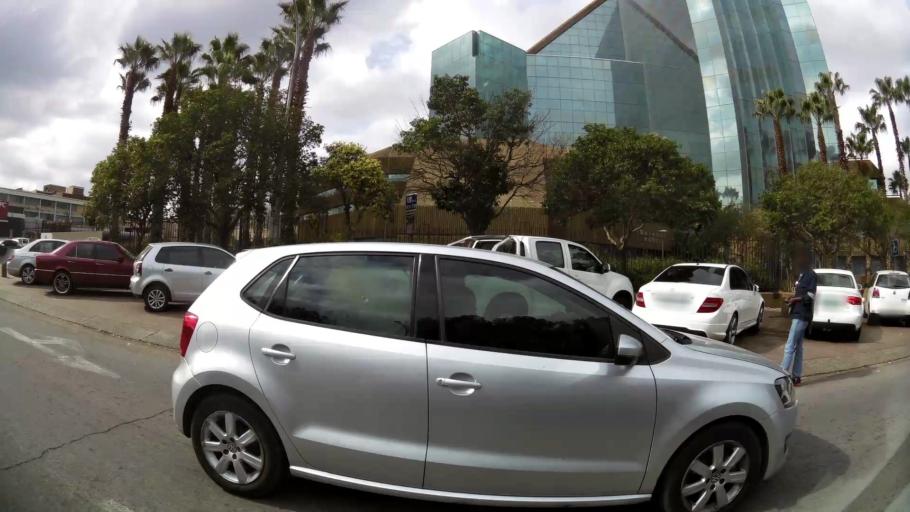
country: ZA
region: Orange Free State
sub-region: Mangaung Metropolitan Municipality
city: Bloemfontein
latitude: -29.1133
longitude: 26.2148
